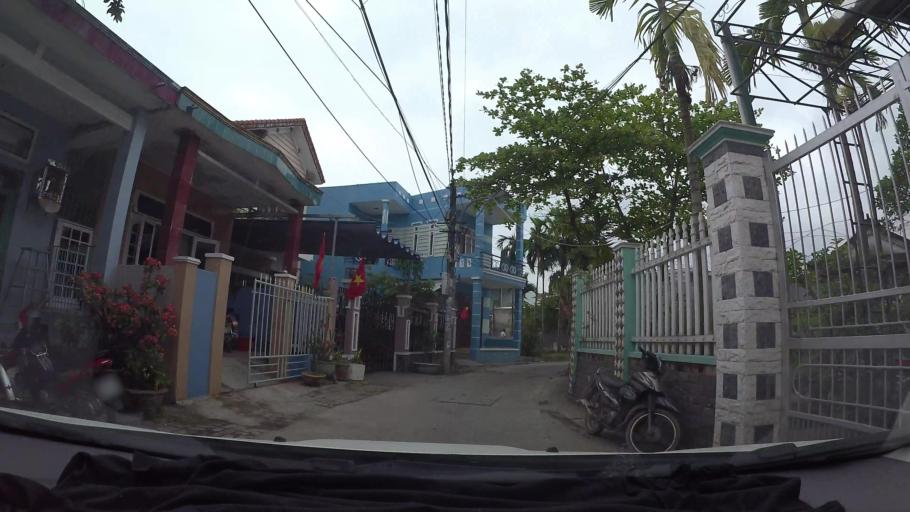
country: VN
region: Da Nang
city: Lien Chieu
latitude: 16.0623
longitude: 108.1680
